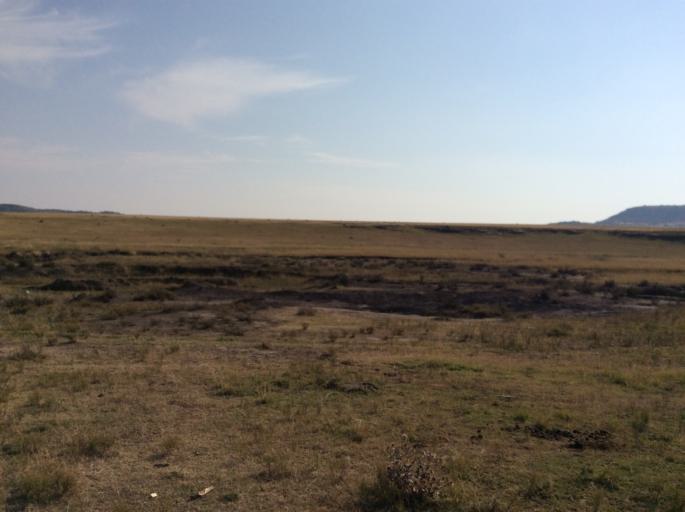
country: LS
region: Mafeteng
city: Mafeteng
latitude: -29.7146
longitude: 27.0053
